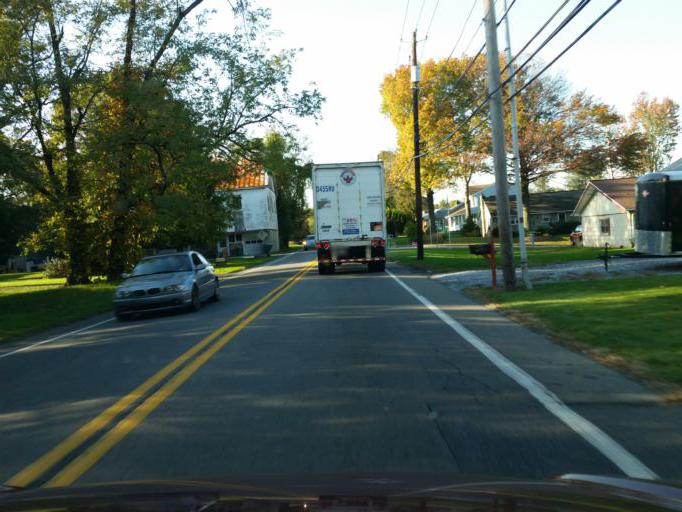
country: US
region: Pennsylvania
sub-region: Dauphin County
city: Hershey
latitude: 40.2634
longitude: -76.6420
